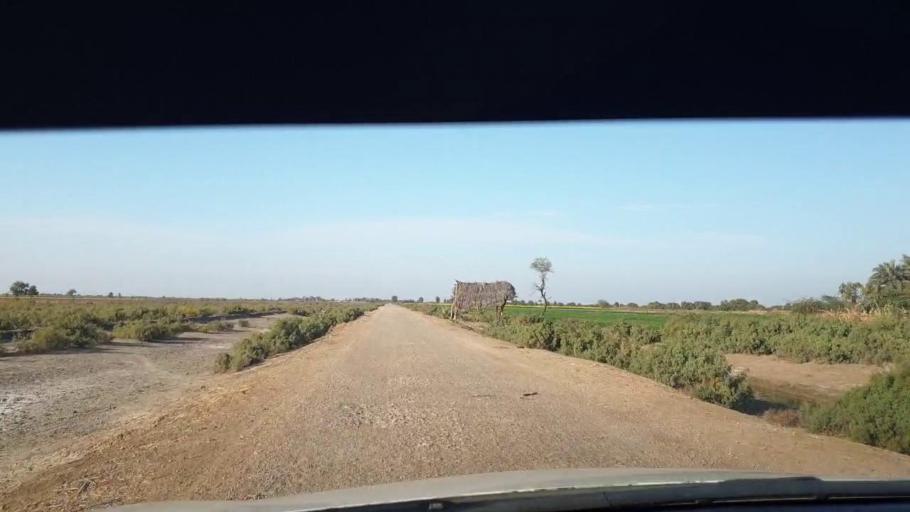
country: PK
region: Sindh
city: Berani
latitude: 25.8094
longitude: 68.9102
